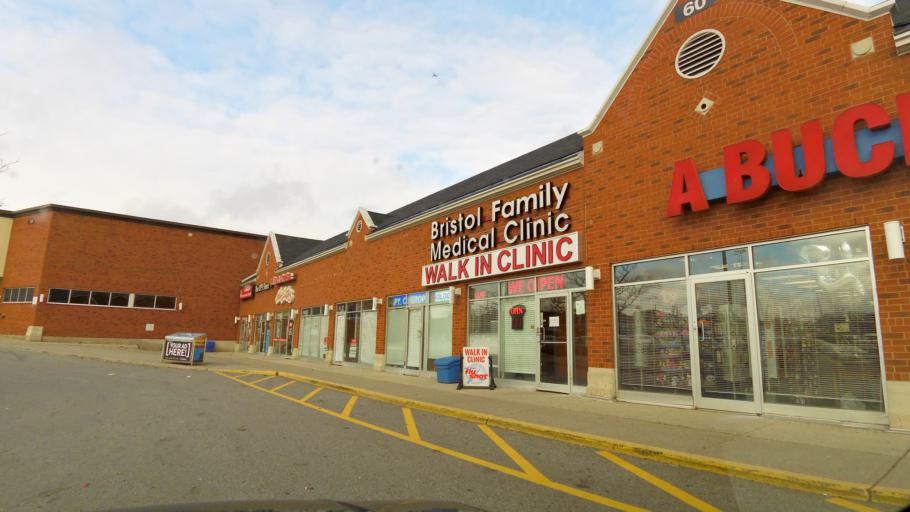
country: CA
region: Ontario
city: Mississauga
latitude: 43.6149
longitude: -79.6609
